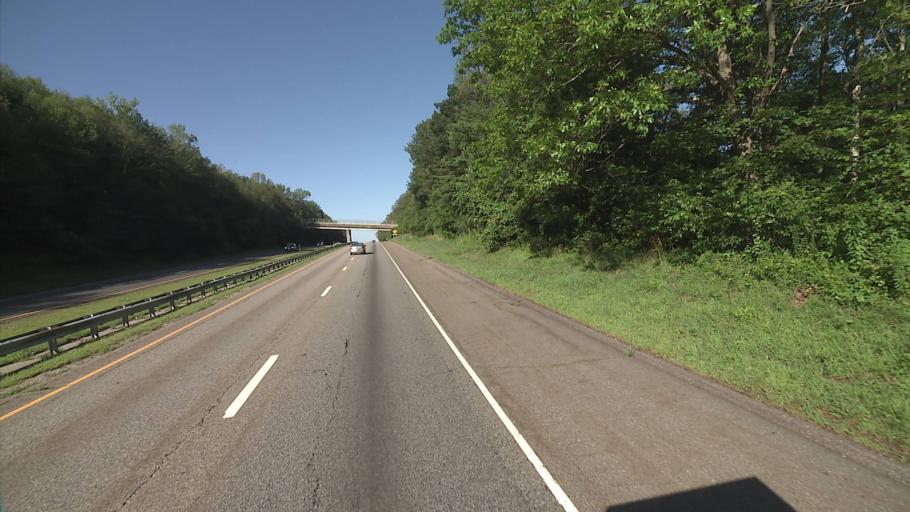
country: US
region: Connecticut
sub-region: New London County
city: Jewett City
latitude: 41.6037
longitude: -71.9541
